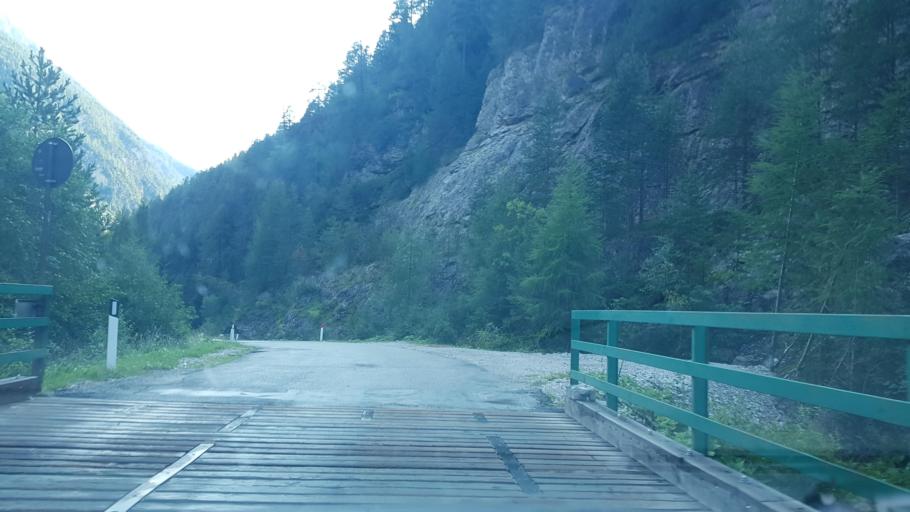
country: IT
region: Veneto
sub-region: Provincia di Belluno
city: San Pietro di Cadore
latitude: 46.5905
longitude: 12.6290
